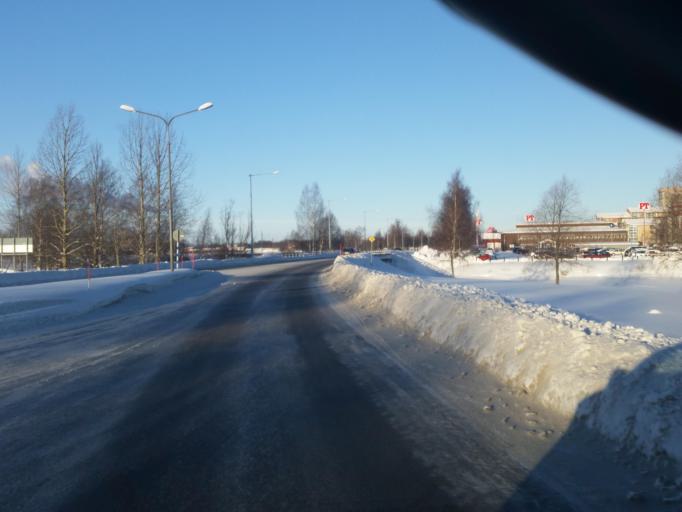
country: SE
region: Norrbotten
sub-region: Pitea Kommun
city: Pitea
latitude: 65.3122
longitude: 21.4872
